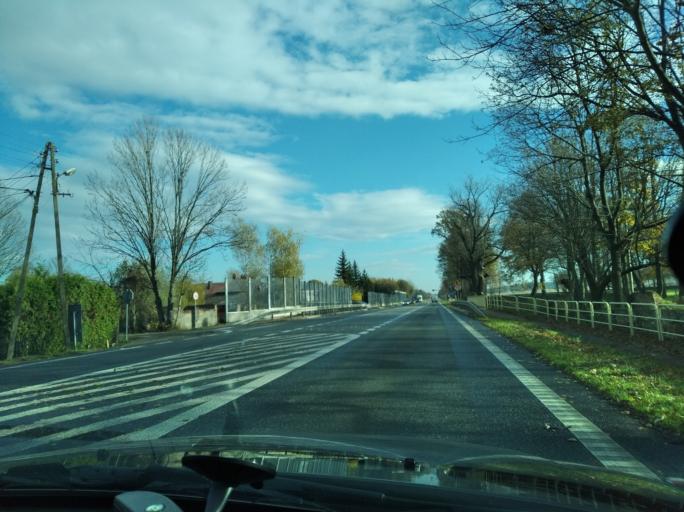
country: PL
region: Subcarpathian Voivodeship
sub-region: Powiat debicki
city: Brzeznica
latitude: 50.0594
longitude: 21.4799
